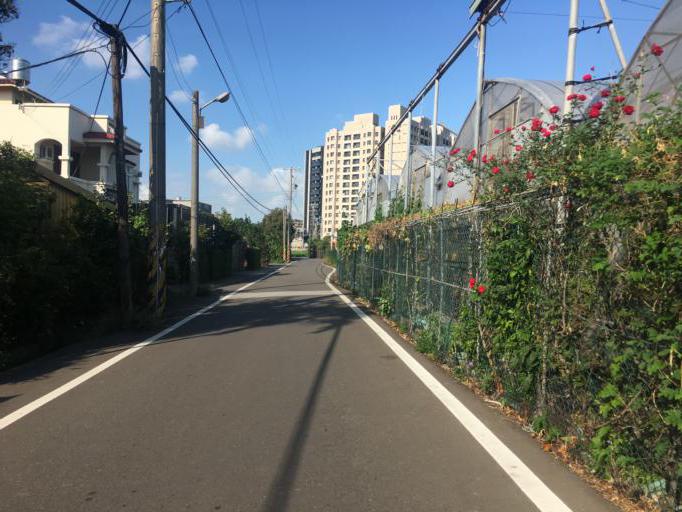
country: TW
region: Taiwan
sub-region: Hsinchu
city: Zhubei
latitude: 24.8392
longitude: 120.9930
